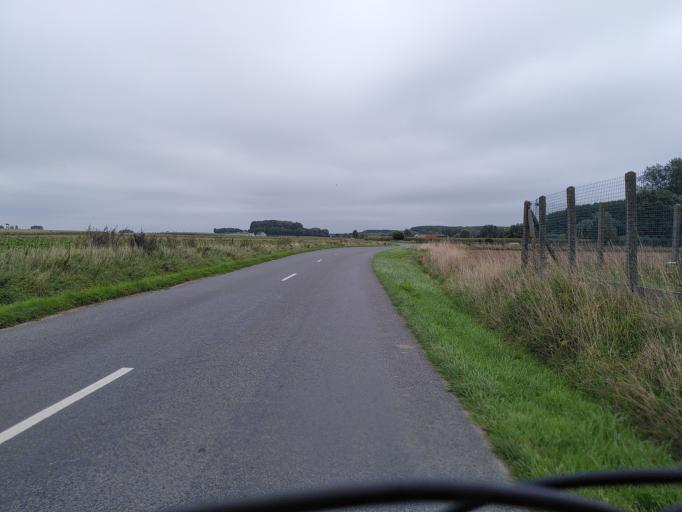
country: FR
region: Nord-Pas-de-Calais
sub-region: Departement du Pas-de-Calais
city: Mametz
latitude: 50.6450
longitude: 2.3144
